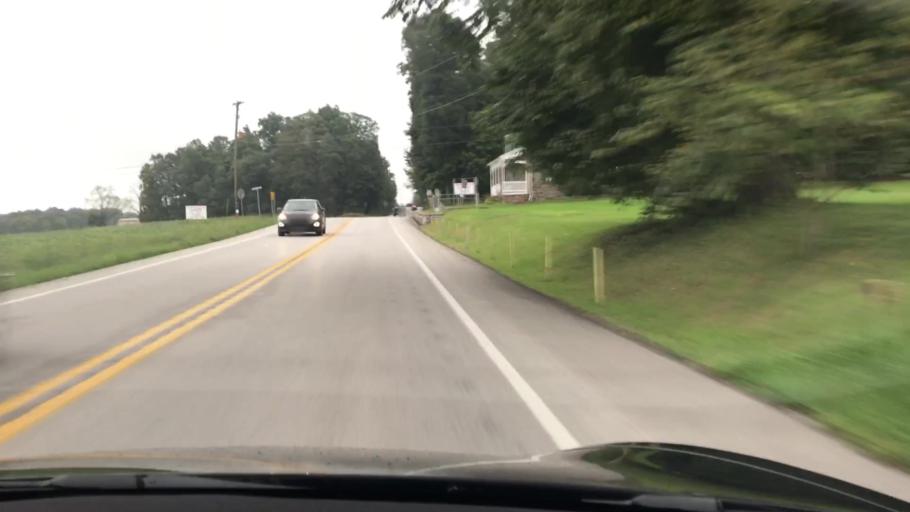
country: US
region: Pennsylvania
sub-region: York County
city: Weigelstown
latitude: 39.9411
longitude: -76.8611
